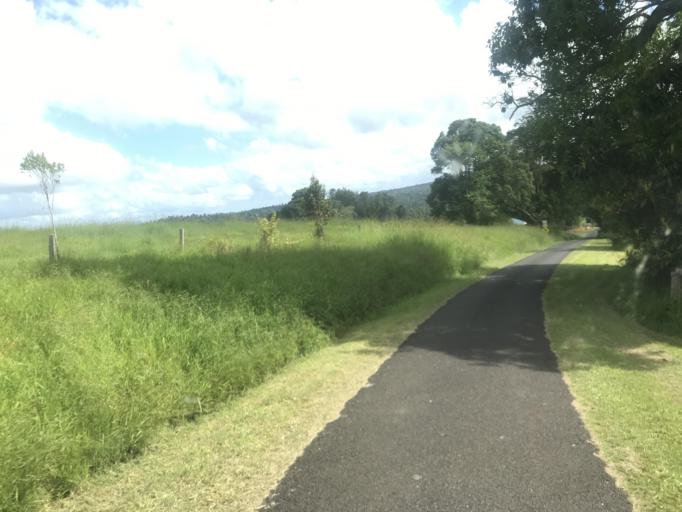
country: AU
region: Queensland
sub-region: Tablelands
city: Ravenshoe
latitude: -17.5473
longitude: 145.6981
